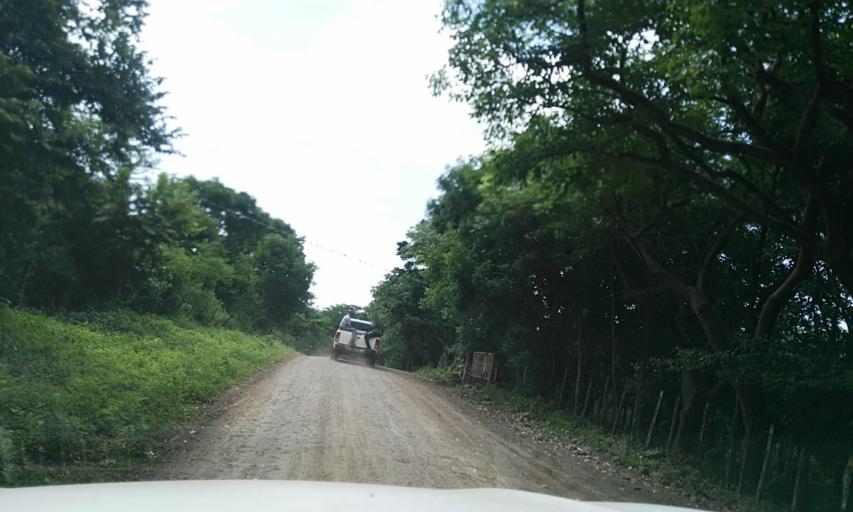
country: NI
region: Matagalpa
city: Terrabona
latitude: 12.7115
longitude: -85.9601
